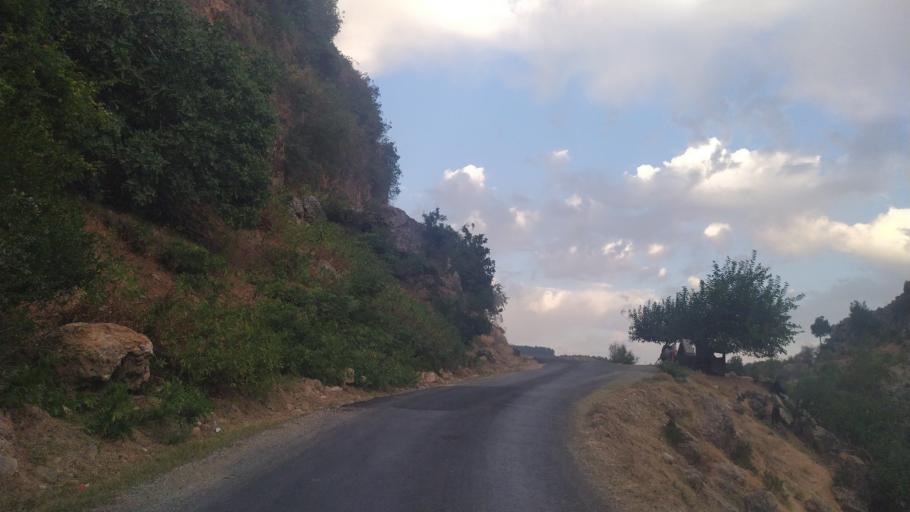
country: TR
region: Mersin
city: Camliyayla
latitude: 37.2389
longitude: 34.7151
